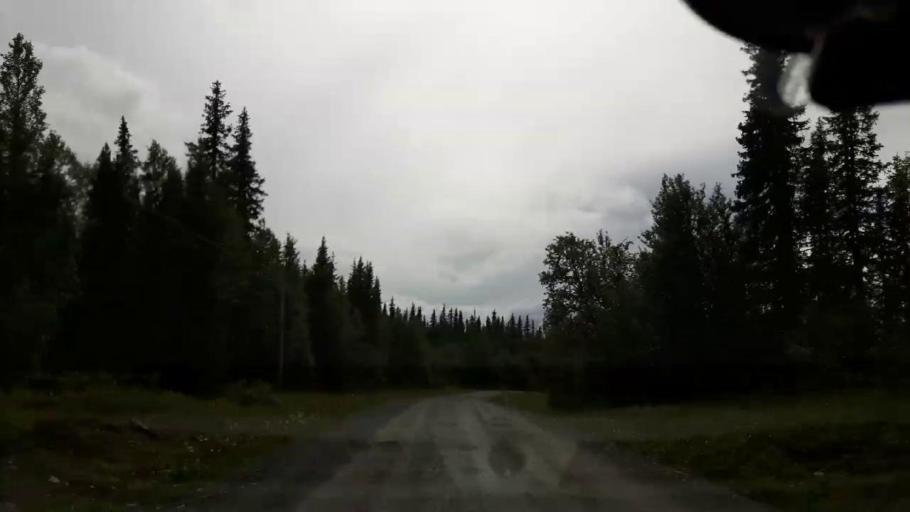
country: SE
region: Jaemtland
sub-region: Krokoms Kommun
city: Valla
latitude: 63.7570
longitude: 13.8376
